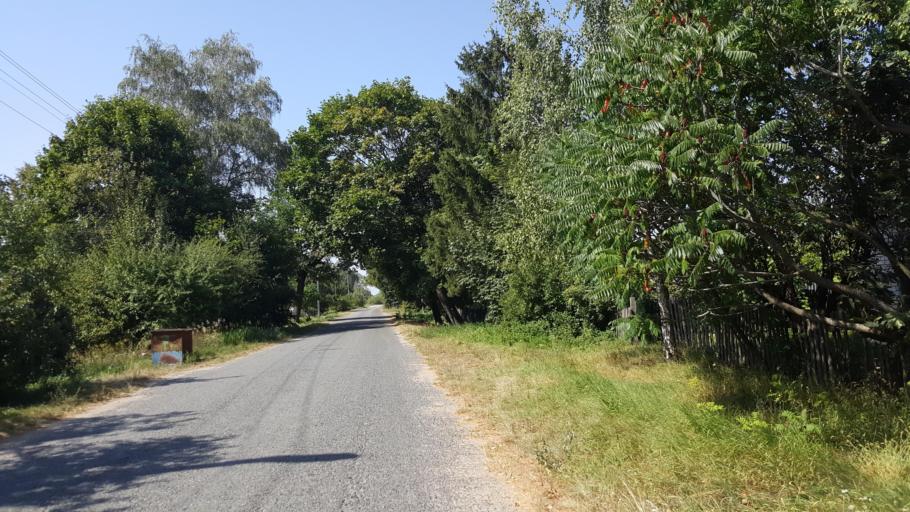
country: BY
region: Brest
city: Vysokaye
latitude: 52.4487
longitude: 23.4493
